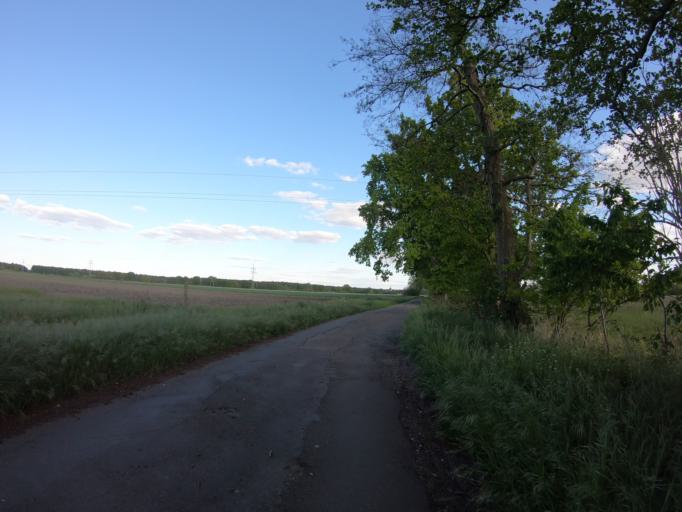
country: DE
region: Lower Saxony
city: Gifhorn
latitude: 52.5025
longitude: 10.5462
